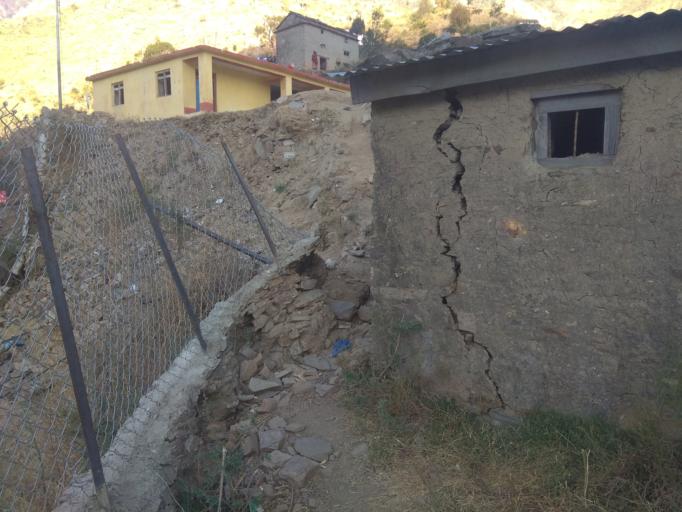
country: NP
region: Mid Western
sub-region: Bheri Zone
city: Dailekh
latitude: 29.2862
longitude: 81.7148
